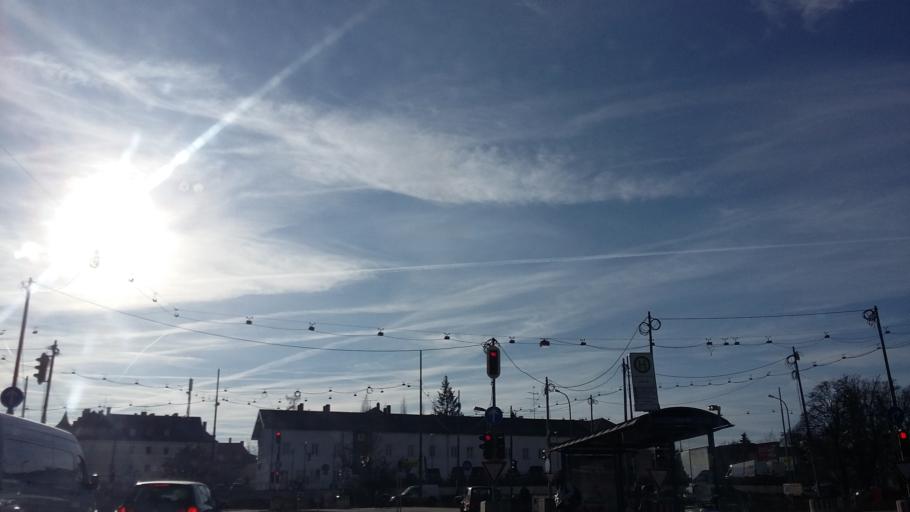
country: DE
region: Bavaria
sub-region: Upper Bavaria
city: Pasing
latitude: 48.1455
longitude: 11.5034
